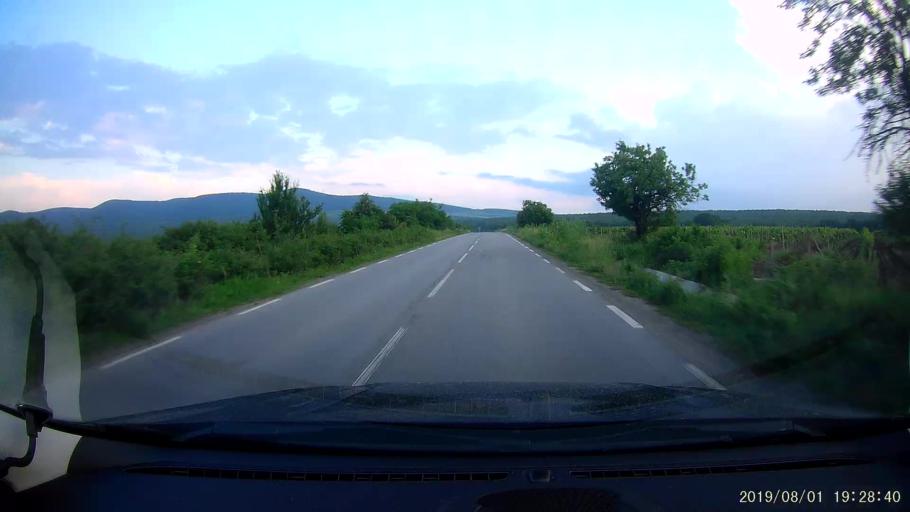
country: BG
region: Burgas
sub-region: Obshtina Sungurlare
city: Sungurlare
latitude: 42.8395
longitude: 26.9142
